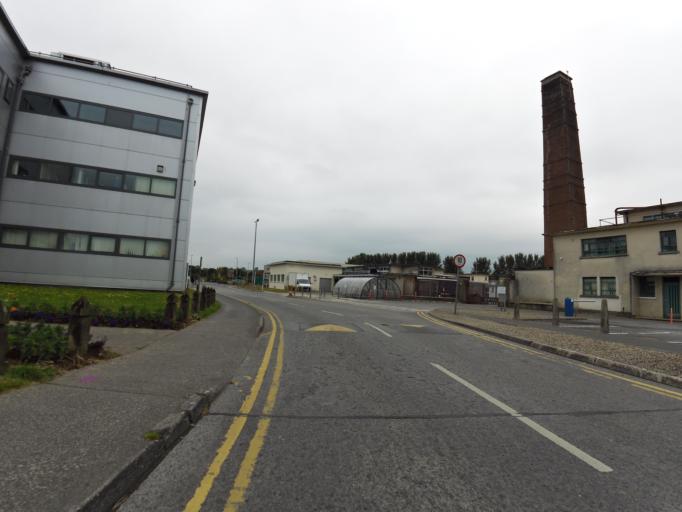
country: IE
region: Connaught
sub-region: County Galway
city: Gaillimh
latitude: 53.2779
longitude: -9.0663
